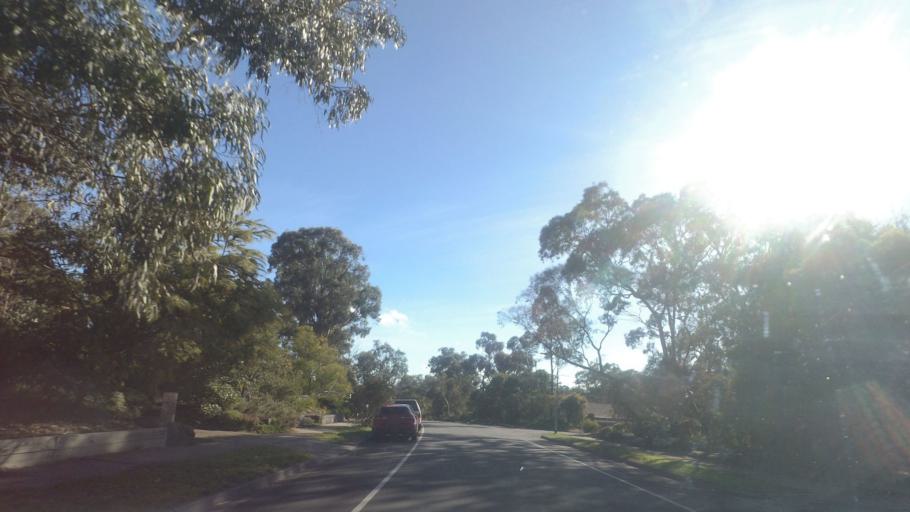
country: AU
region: Victoria
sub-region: Nillumbik
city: Eltham North
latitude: -37.7126
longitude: 145.1611
